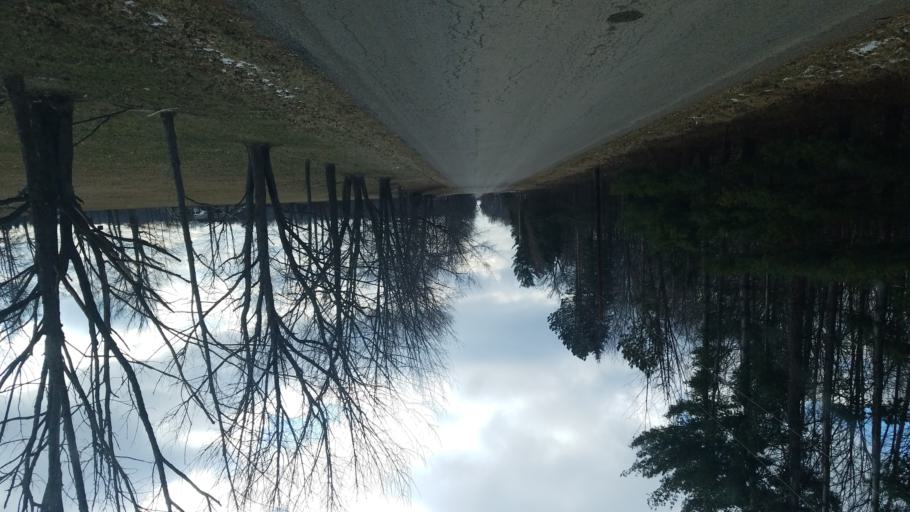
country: US
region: Ohio
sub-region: Crawford County
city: Galion
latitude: 40.6473
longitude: -82.7469
